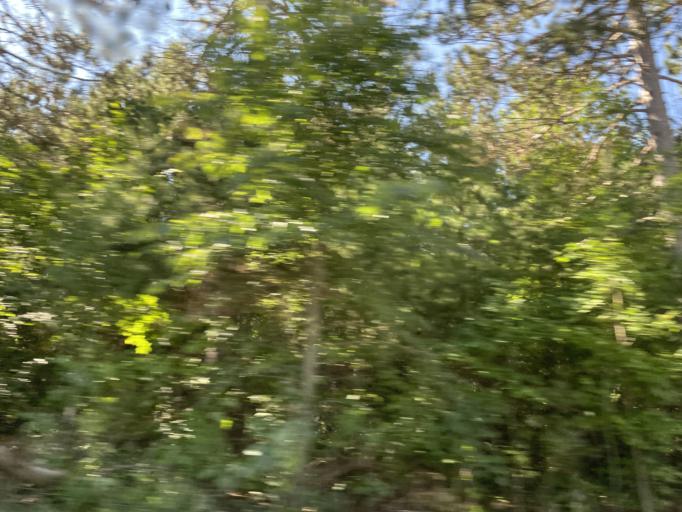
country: US
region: Michigan
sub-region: Benzie County
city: Beulah
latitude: 44.6172
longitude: -86.0527
